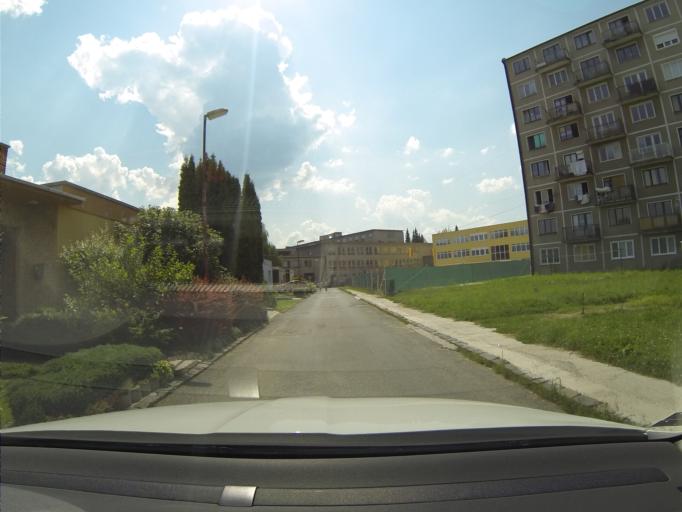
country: SK
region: Nitriansky
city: Prievidza
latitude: 48.7772
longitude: 18.6102
